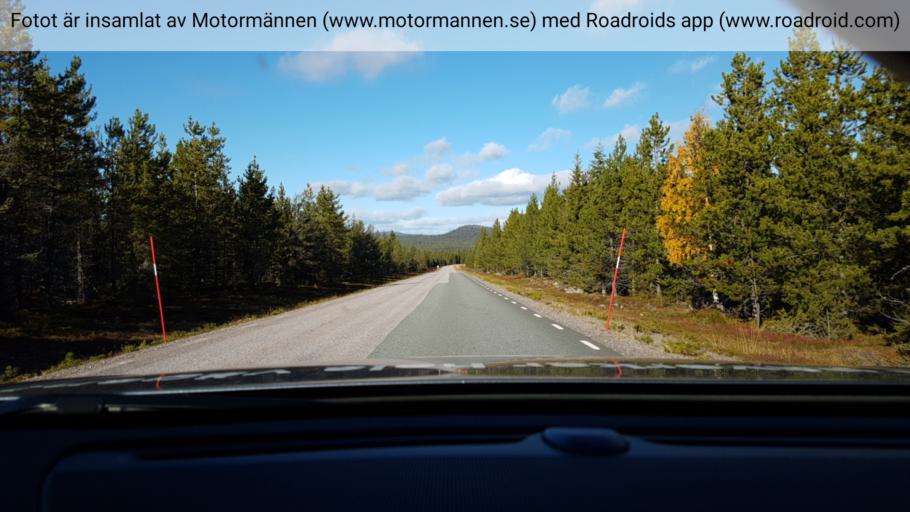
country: SE
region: Norrbotten
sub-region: Arjeplogs Kommun
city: Arjeplog
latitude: 65.8429
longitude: 18.4139
